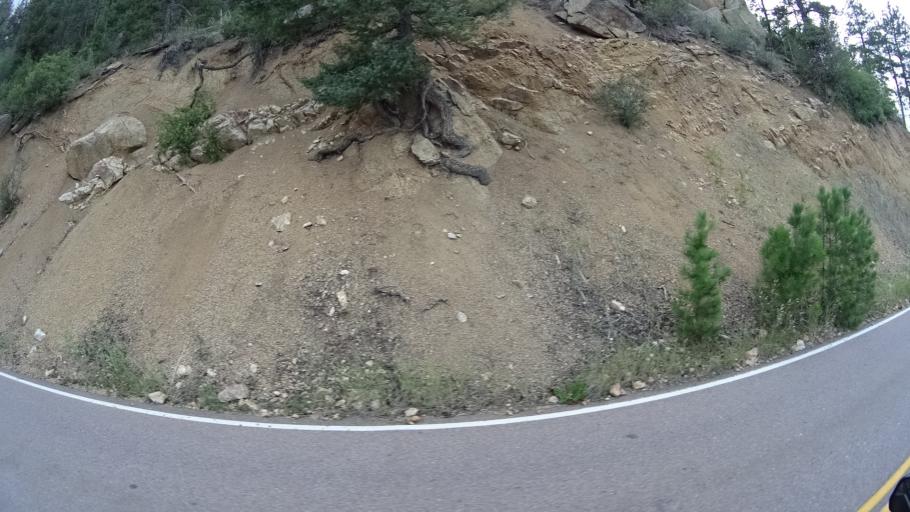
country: US
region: Colorado
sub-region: El Paso County
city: Cascade-Chipita Park
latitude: 38.9004
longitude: -104.9799
